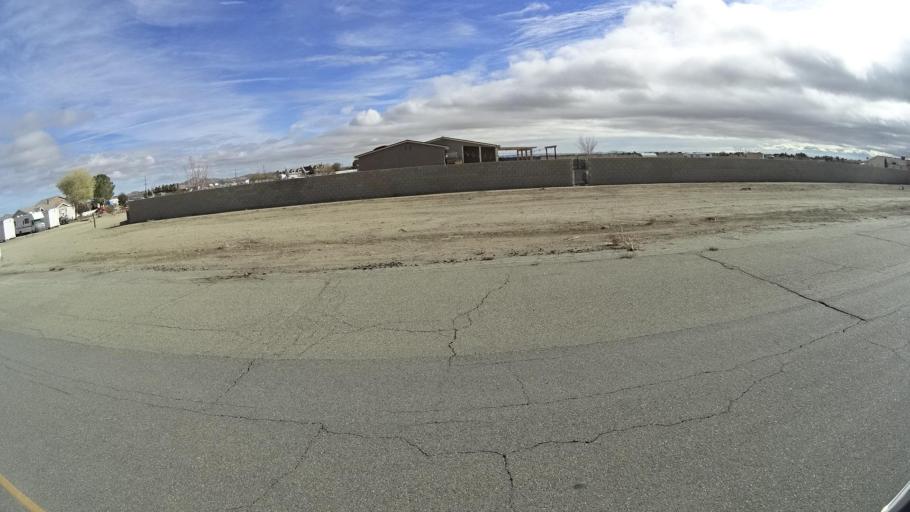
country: US
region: California
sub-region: Kern County
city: Rosamond
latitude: 34.8324
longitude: -118.2731
